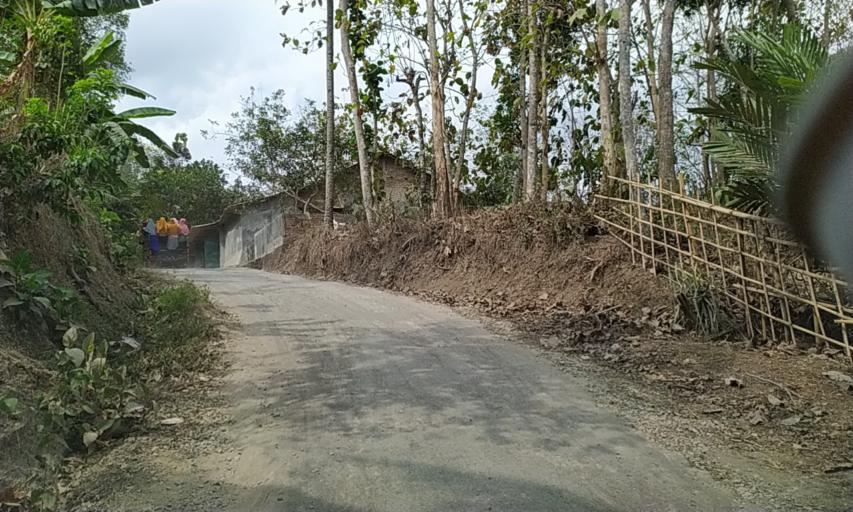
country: ID
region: Central Java
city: Genteng Wetan
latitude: -7.3628
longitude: 108.8864
